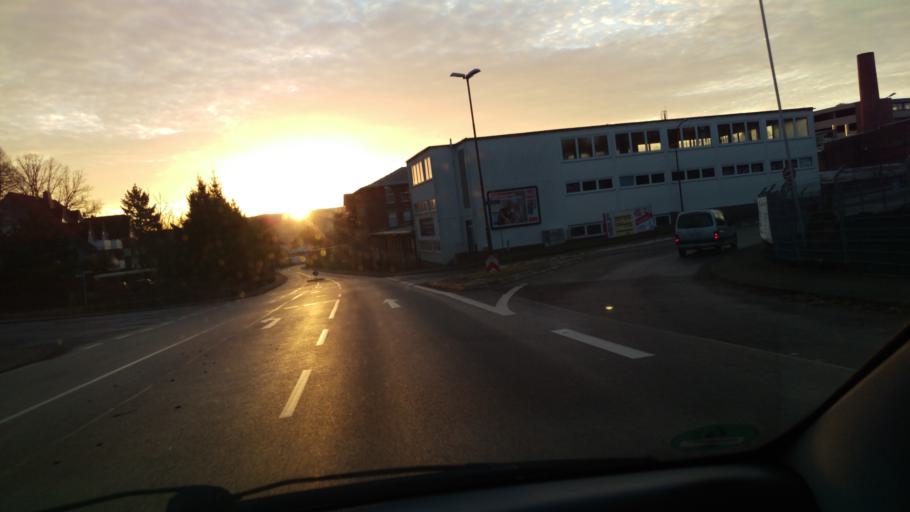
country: DE
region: Hesse
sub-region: Regierungsbezirk Giessen
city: Alsfeld
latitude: 50.7548
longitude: 9.2629
